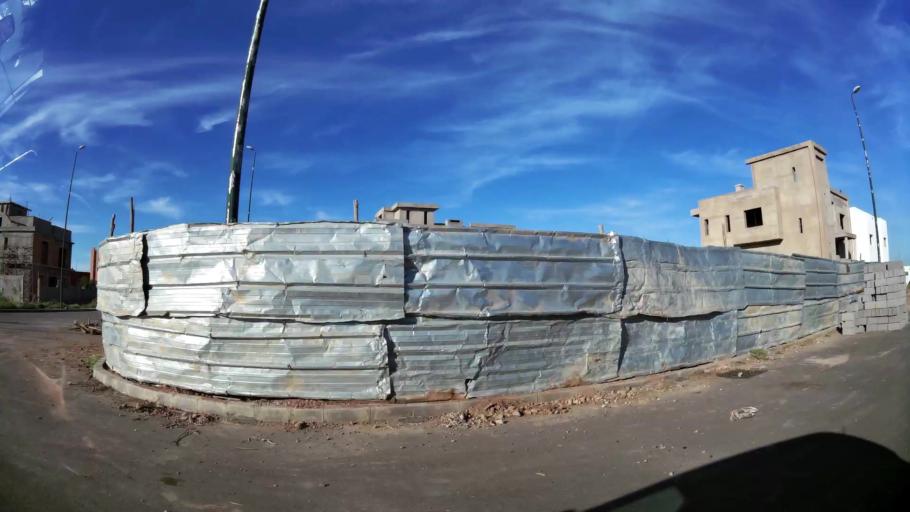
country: MA
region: Marrakech-Tensift-Al Haouz
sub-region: Marrakech
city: Marrakesh
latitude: 31.6699
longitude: -8.0734
